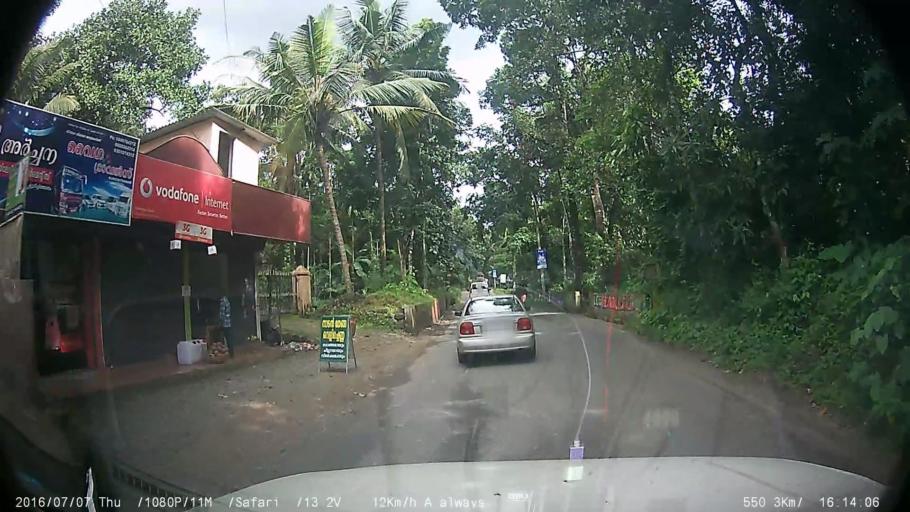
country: IN
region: Kerala
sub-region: Kottayam
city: Palackattumala
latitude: 9.7705
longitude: 76.6105
